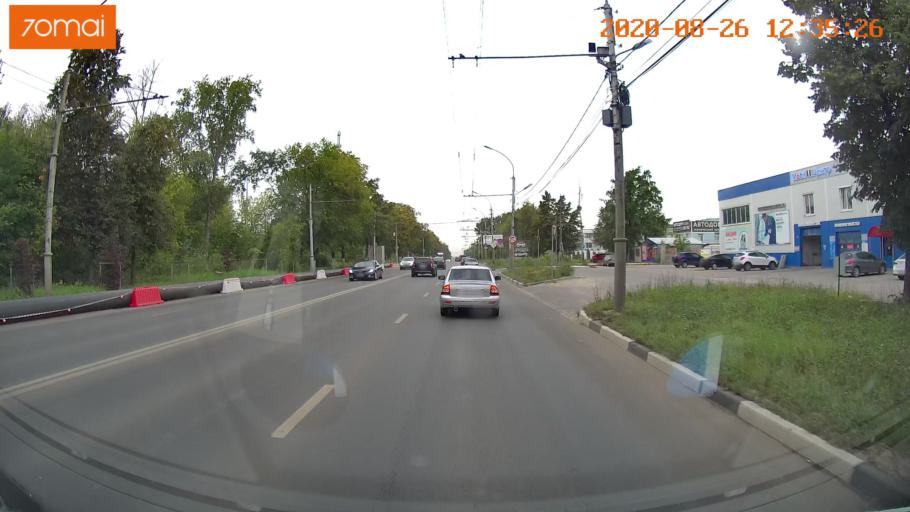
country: RU
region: Rjazan
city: Ryazan'
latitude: 54.5958
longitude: 39.7682
